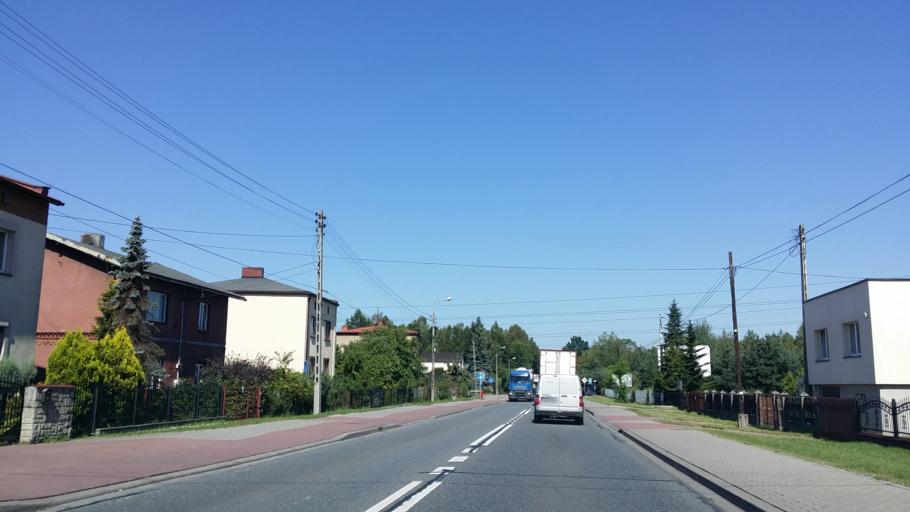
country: PL
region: Silesian Voivodeship
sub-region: Powiat bierunsko-ledzinski
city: Imielin
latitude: 50.1567
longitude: 19.1783
